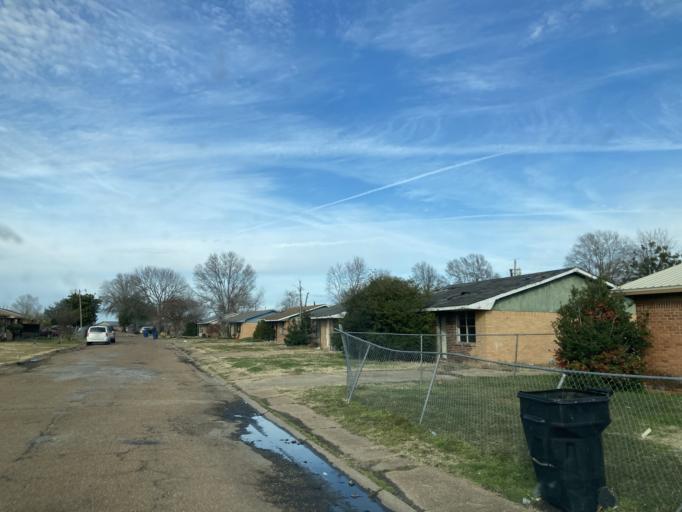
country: US
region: Mississippi
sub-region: Humphreys County
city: Belzoni
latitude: 33.1703
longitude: -90.5010
